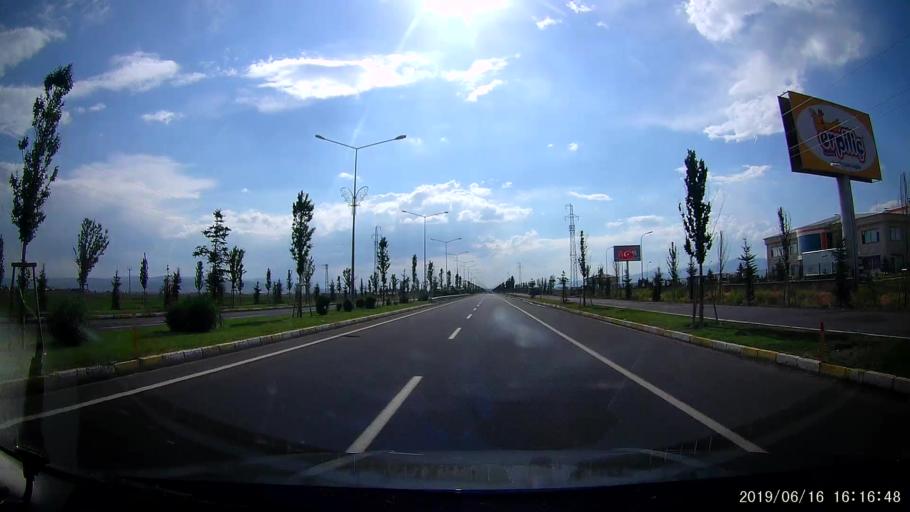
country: TR
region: Erzurum
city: Ilica
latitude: 39.9632
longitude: 41.2005
